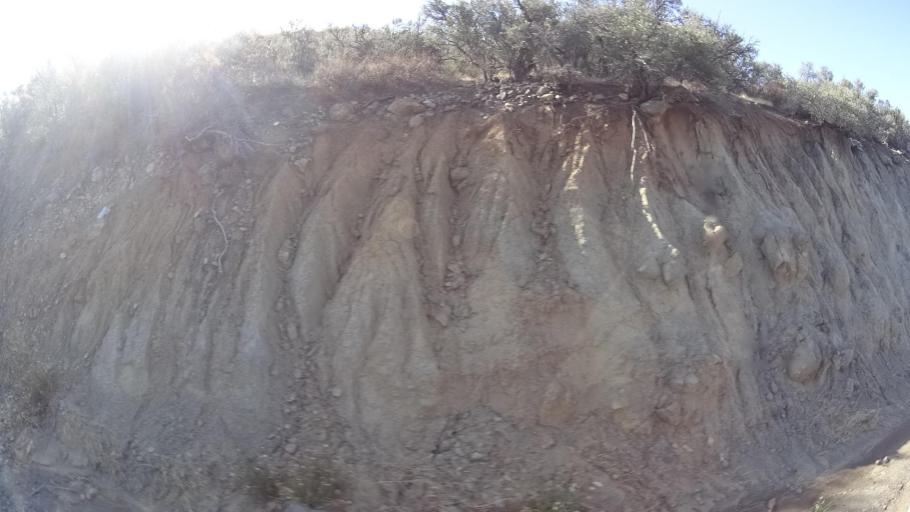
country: US
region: California
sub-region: San Diego County
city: Pine Valley
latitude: 32.8221
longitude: -116.5078
